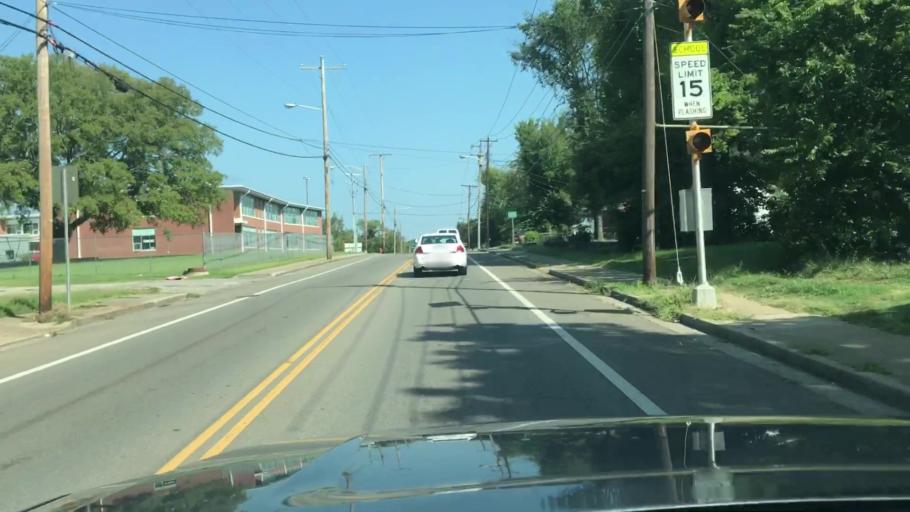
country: US
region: Tennessee
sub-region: Davidson County
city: Nashville
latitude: 36.1745
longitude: -86.8087
